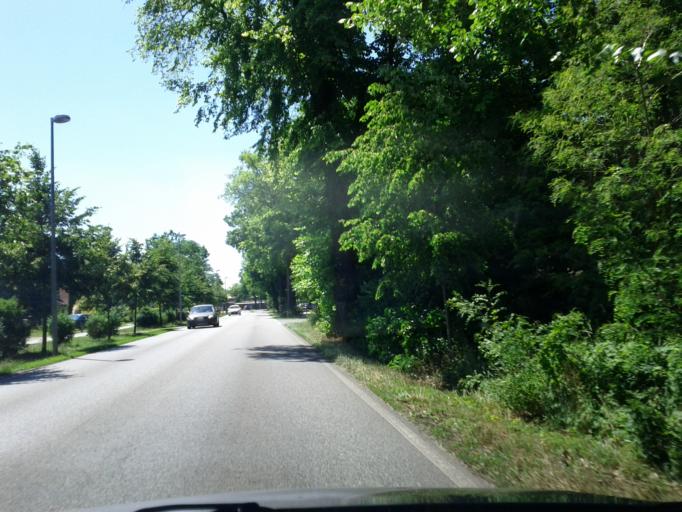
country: DE
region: Brandenburg
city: Erkner
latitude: 52.4317
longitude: 13.7527
